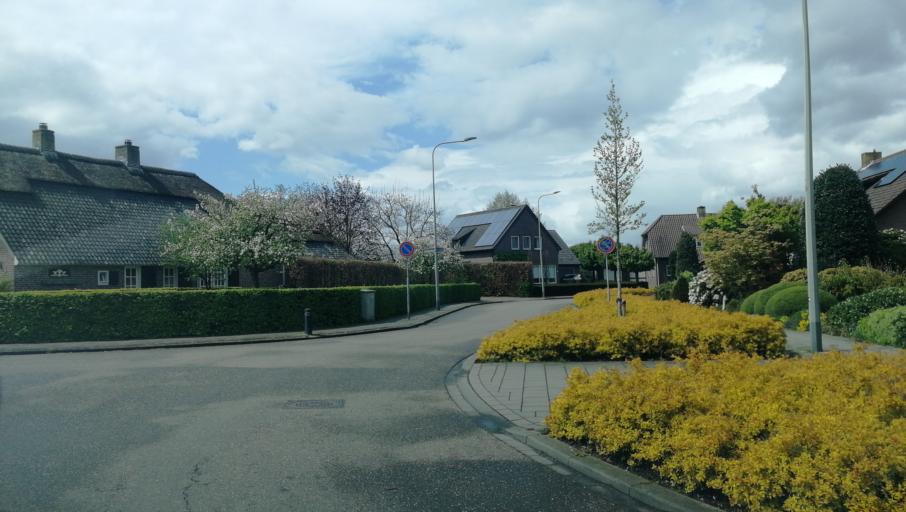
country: NL
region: Limburg
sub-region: Gemeente Peel en Maas
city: Maasbree
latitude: 51.4081
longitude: 6.0326
